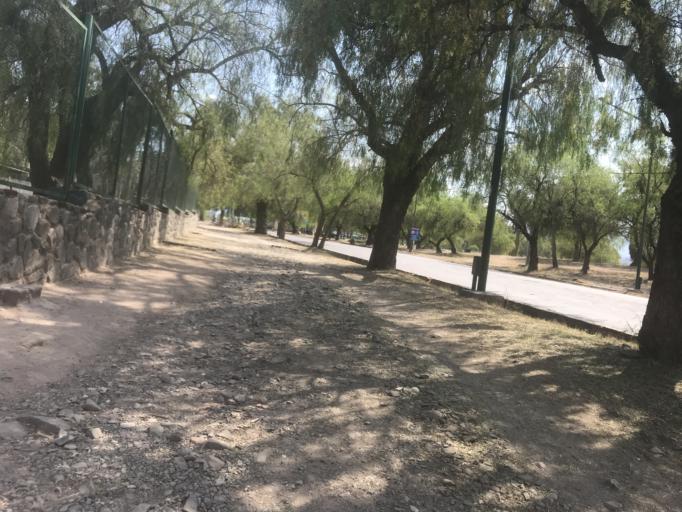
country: AR
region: Mendoza
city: Mendoza
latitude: -32.8834
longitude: -68.8878
